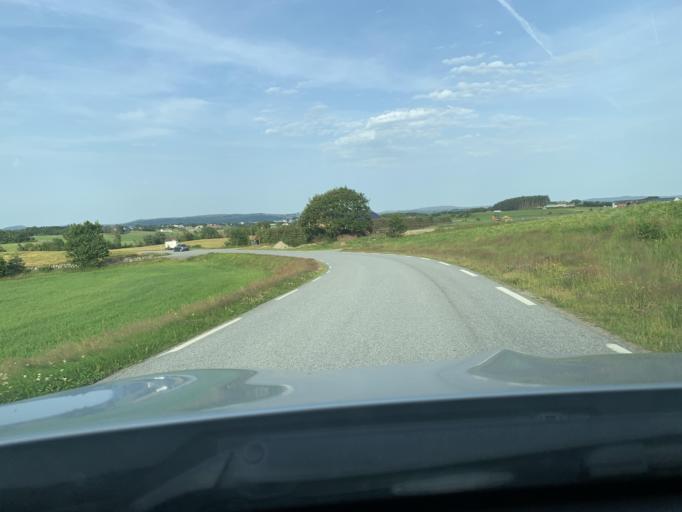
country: NO
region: Rogaland
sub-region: Time
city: Bryne
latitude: 58.7330
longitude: 5.5972
